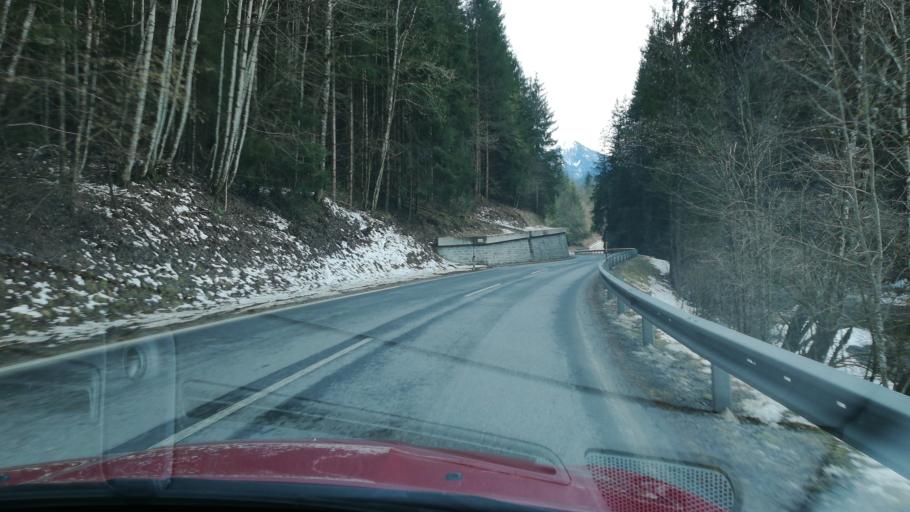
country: AT
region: Styria
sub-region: Politischer Bezirk Liezen
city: Irdning
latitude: 47.4853
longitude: 14.1127
